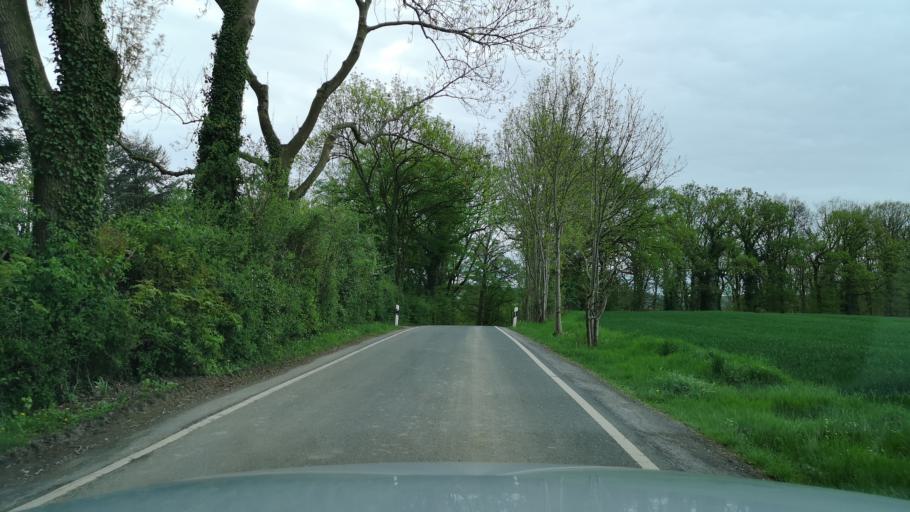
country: DE
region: North Rhine-Westphalia
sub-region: Regierungsbezirk Arnsberg
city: Frondenberg
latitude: 51.4459
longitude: 7.7104
